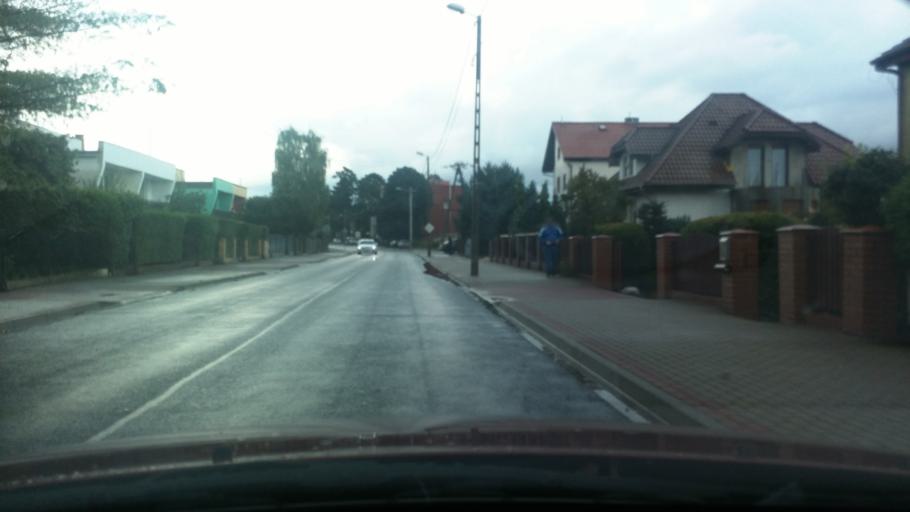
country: PL
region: Lower Silesian Voivodeship
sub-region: Powiat zgorzelecki
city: Zgorzelec
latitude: 51.1363
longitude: 15.0168
